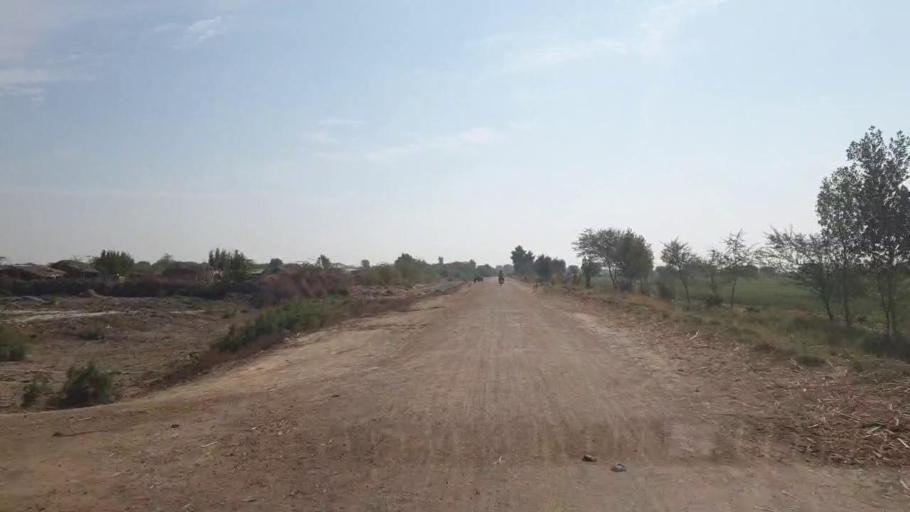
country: PK
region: Sindh
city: Mirwah Gorchani
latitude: 25.3630
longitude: 69.1985
